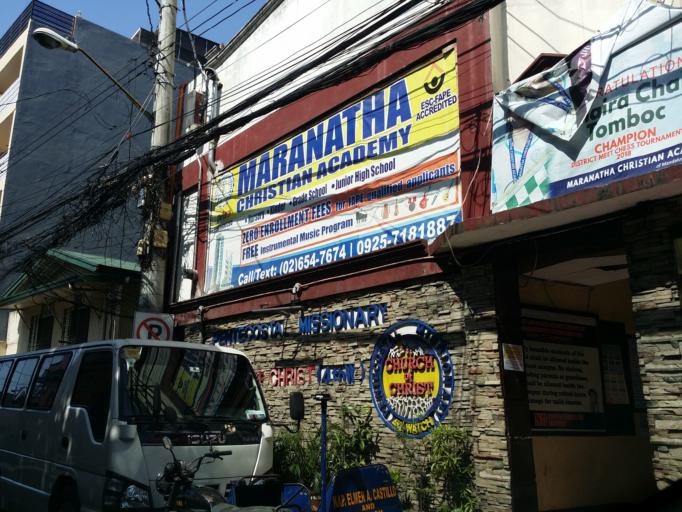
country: PH
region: Metro Manila
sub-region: San Juan
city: San Juan
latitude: 14.5881
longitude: 121.0266
